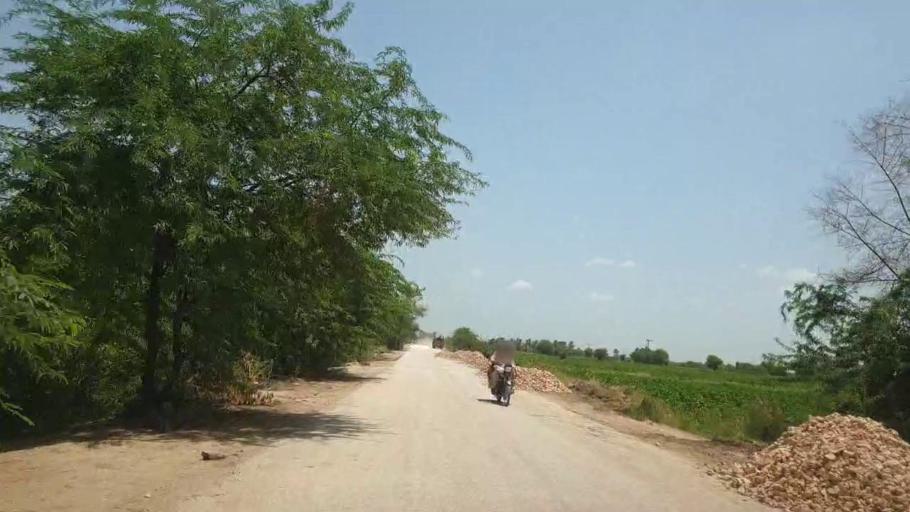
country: PK
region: Sindh
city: Pano Aqil
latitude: 27.6633
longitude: 69.1725
